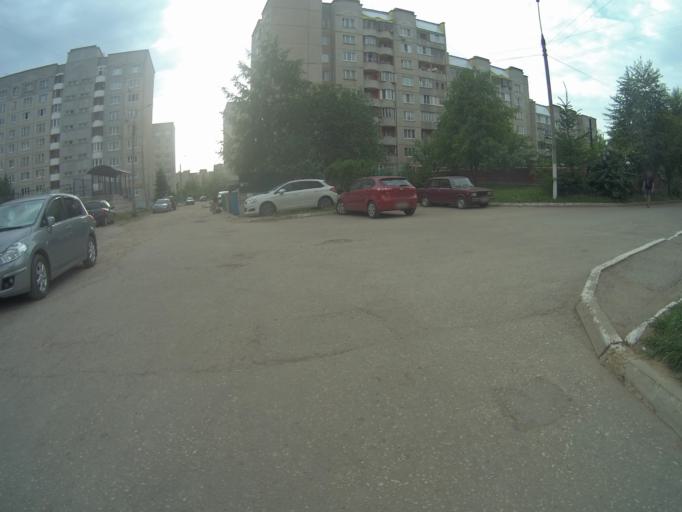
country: RU
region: Vladimir
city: Kommunar
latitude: 56.1626
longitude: 40.4627
